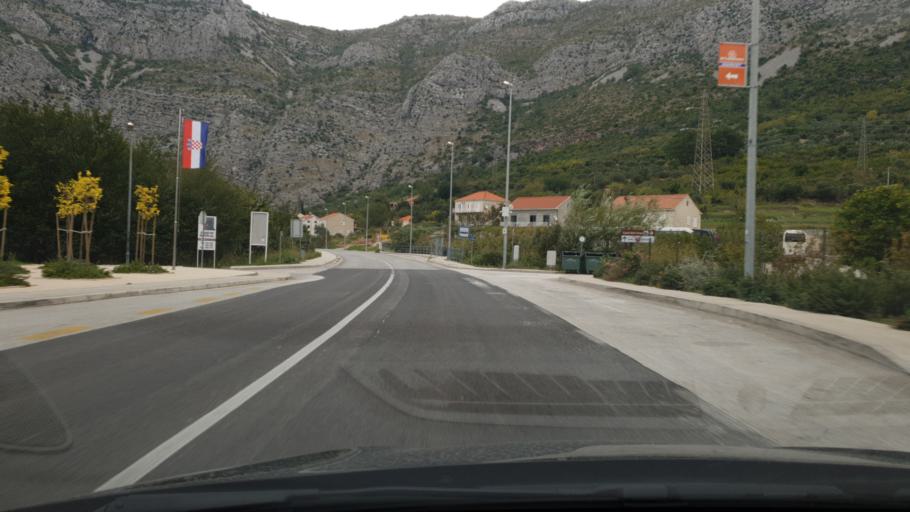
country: HR
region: Dubrovacko-Neretvanska
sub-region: Grad Dubrovnik
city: Mokosica
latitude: 42.6697
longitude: 18.1343
